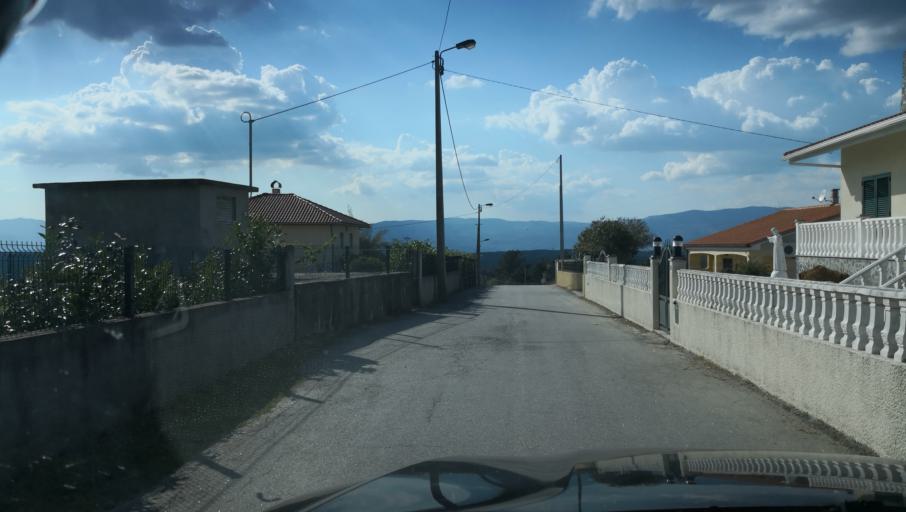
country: PT
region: Vila Real
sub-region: Sabrosa
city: Vilela
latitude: 41.2538
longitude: -7.6599
